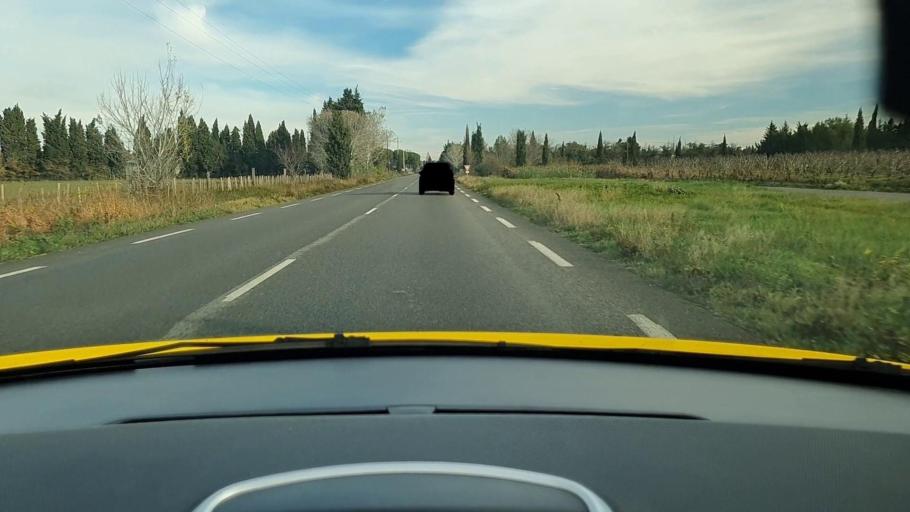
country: FR
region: Languedoc-Roussillon
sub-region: Departement du Gard
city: Beaucaire
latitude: 43.7814
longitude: 4.6245
